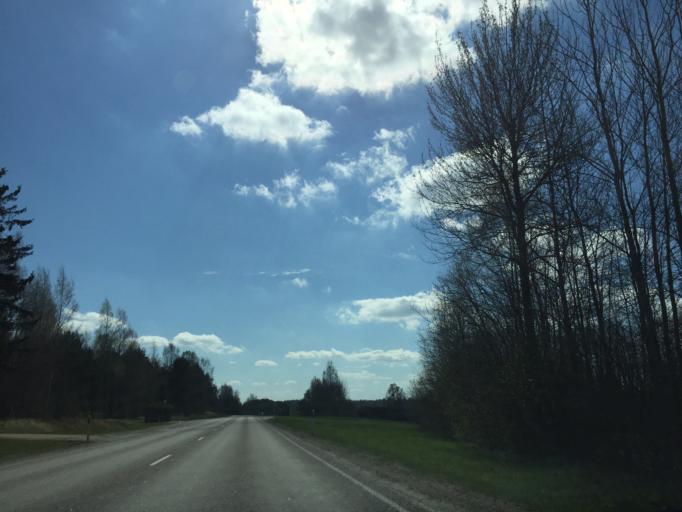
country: EE
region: Tartu
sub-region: Elva linn
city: Elva
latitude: 58.0945
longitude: 26.2271
